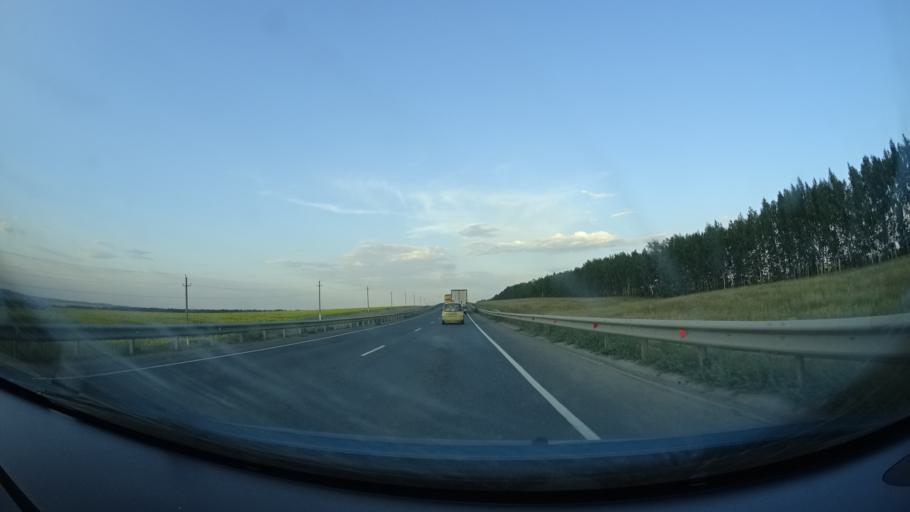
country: RU
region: Samara
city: Kamyshla
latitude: 54.0769
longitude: 52.3124
